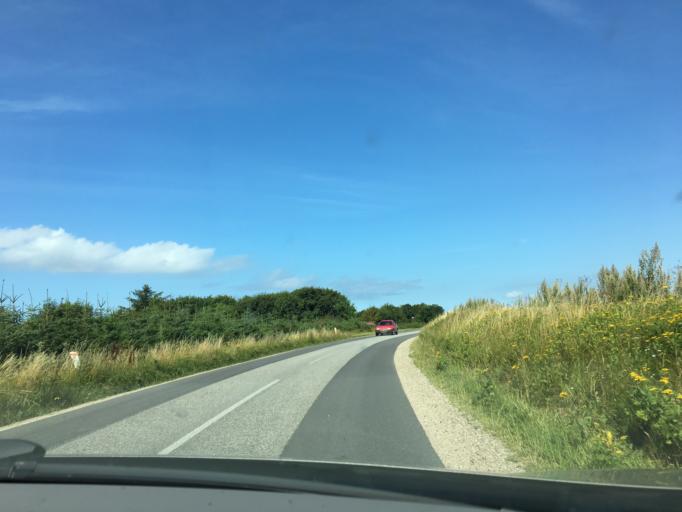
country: DK
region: Central Jutland
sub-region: Ringkobing-Skjern Kommune
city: Ringkobing
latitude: 55.9850
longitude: 8.3408
